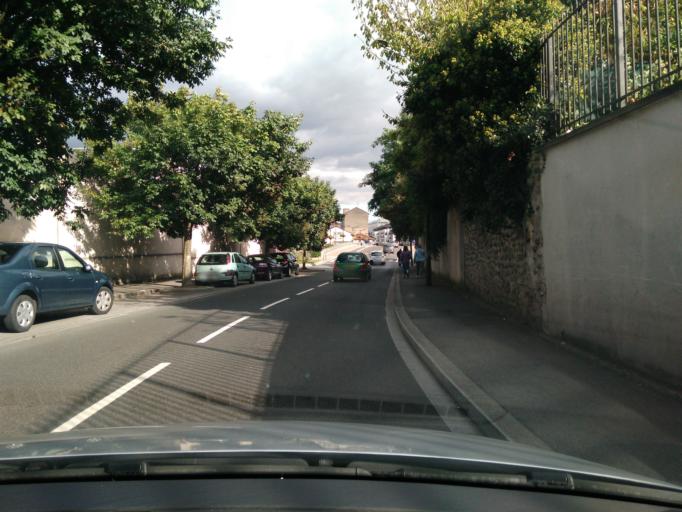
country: FR
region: Ile-de-France
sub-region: Departement de Seine-et-Marne
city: Meaux
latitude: 48.9531
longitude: 2.8804
